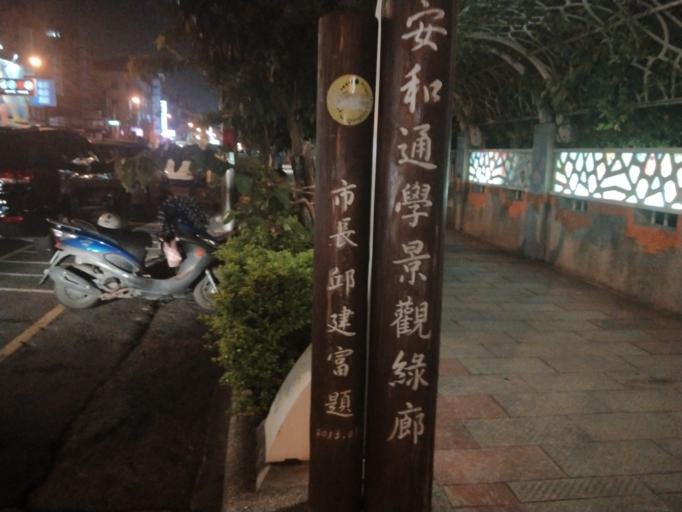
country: TW
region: Taiwan
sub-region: Changhua
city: Chang-hua
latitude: 24.0722
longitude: 120.5361
